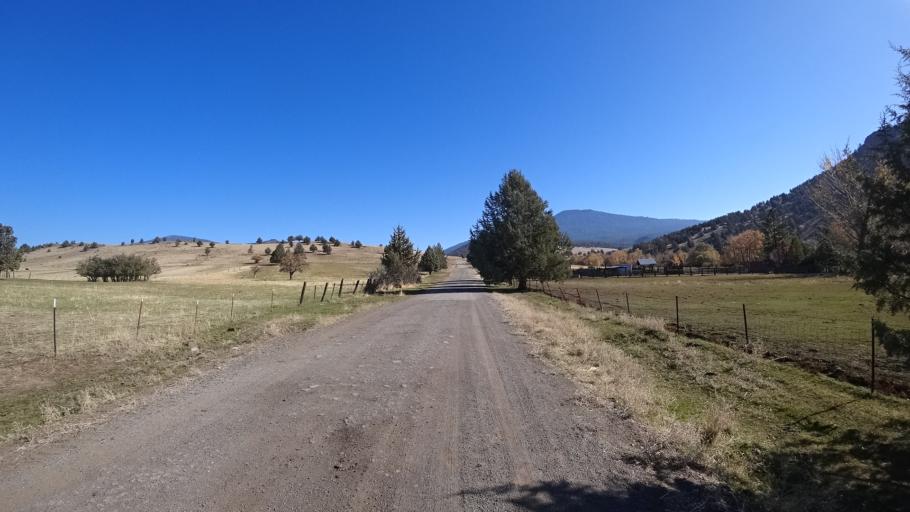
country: US
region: California
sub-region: Siskiyou County
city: Montague
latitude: 41.7398
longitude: -122.3392
